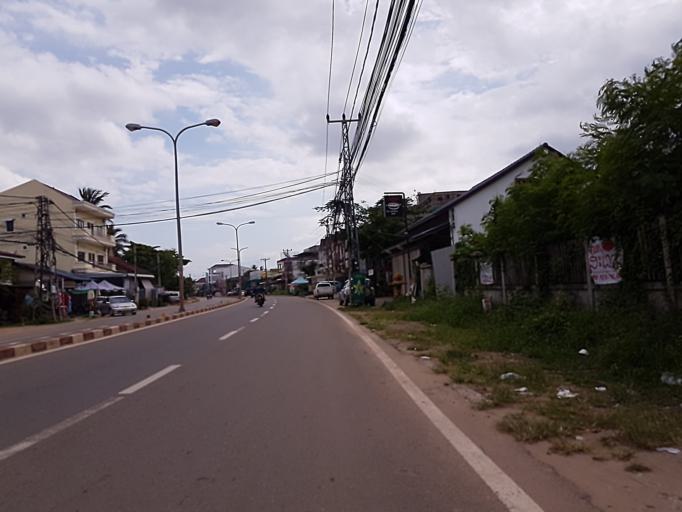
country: TH
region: Nong Khai
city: Si Chiang Mai
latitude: 17.9272
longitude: 102.6164
